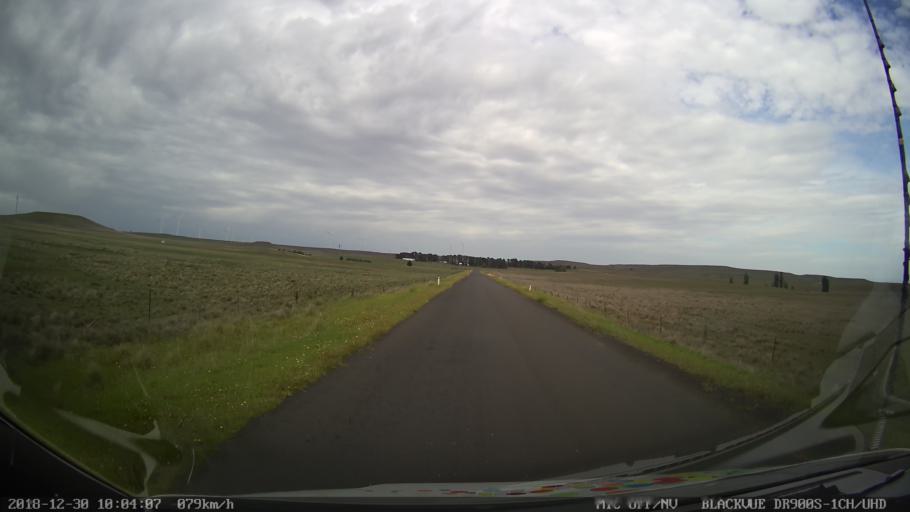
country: AU
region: New South Wales
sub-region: Cooma-Monaro
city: Cooma
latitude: -36.5192
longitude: 149.1495
